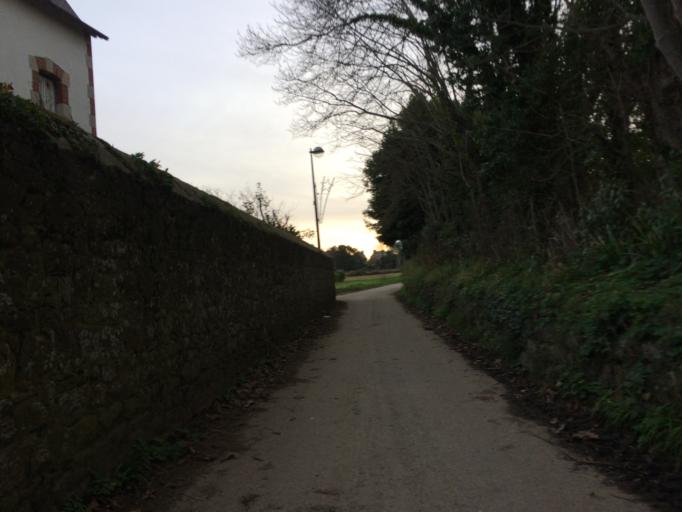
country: FR
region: Brittany
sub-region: Departement des Cotes-d'Armor
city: Ploubazlanec
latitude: 48.8500
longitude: -2.9983
